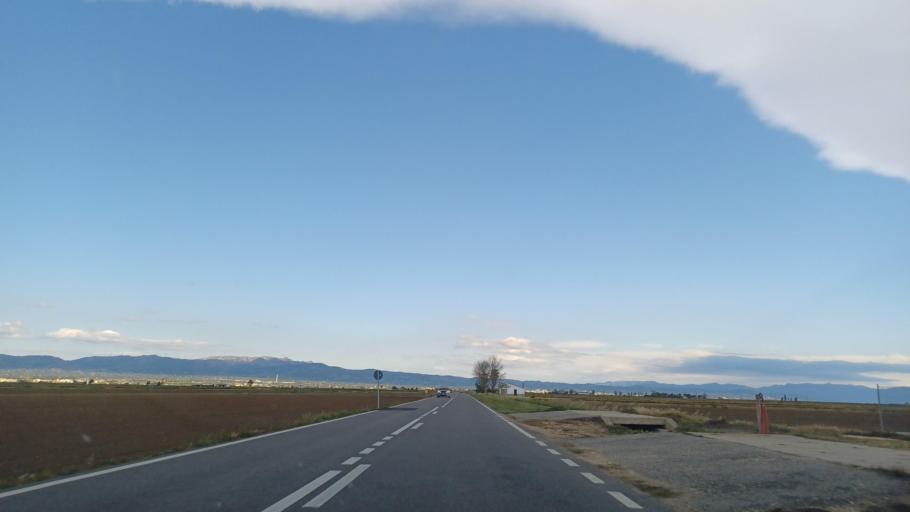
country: ES
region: Catalonia
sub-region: Provincia de Tarragona
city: Deltebre
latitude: 40.7410
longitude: 0.7124
